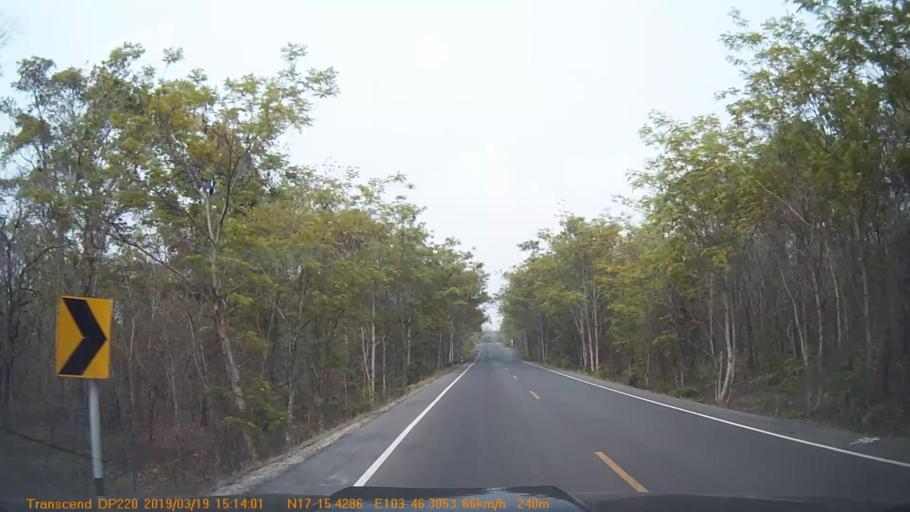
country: TH
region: Sakon Nakhon
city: Nikhom Nam Un
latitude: 17.2573
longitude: 103.7721
